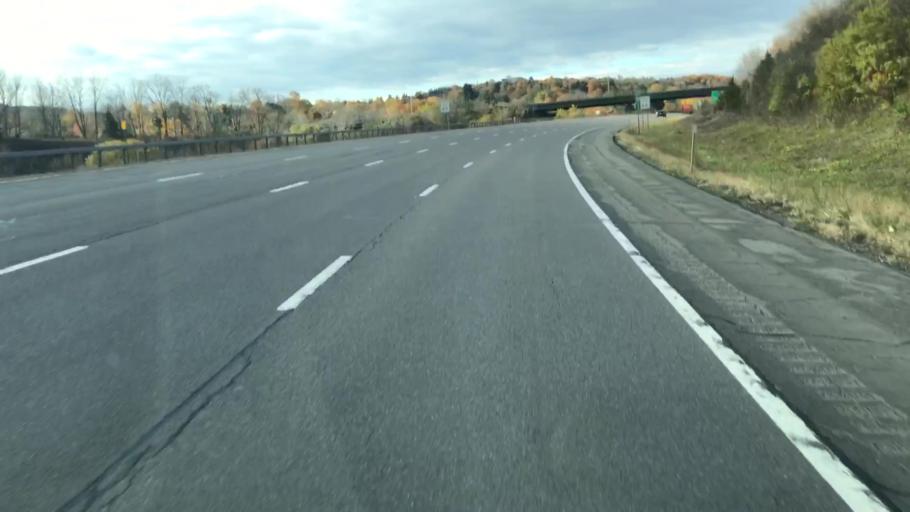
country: US
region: New York
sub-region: Onondaga County
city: Fairmount
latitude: 43.0544
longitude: -76.2403
